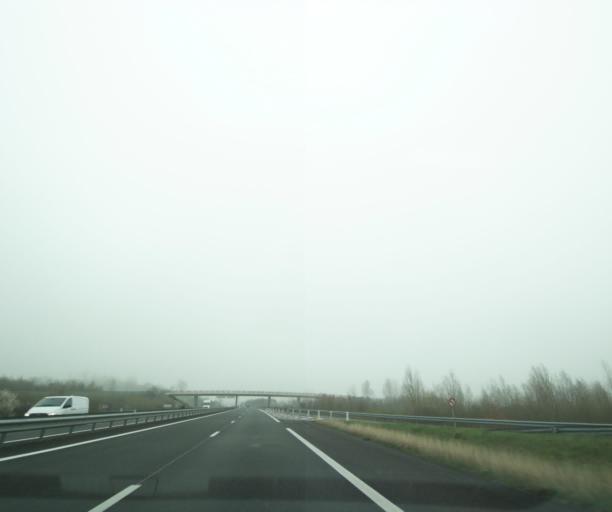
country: FR
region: Midi-Pyrenees
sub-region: Departement du Tarn-et-Garonne
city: Caussade
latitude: 44.1541
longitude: 1.5147
